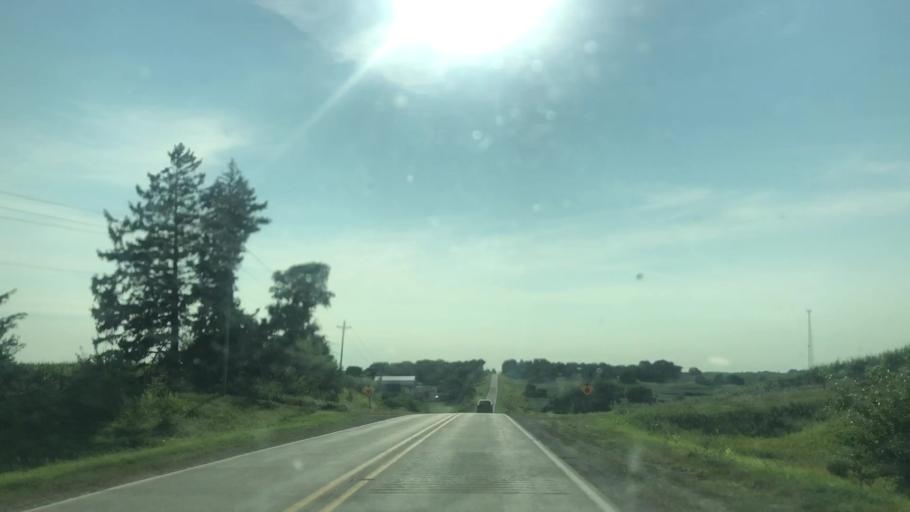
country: US
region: Iowa
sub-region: Marshall County
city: Marshalltown
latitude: 42.0488
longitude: -92.9974
